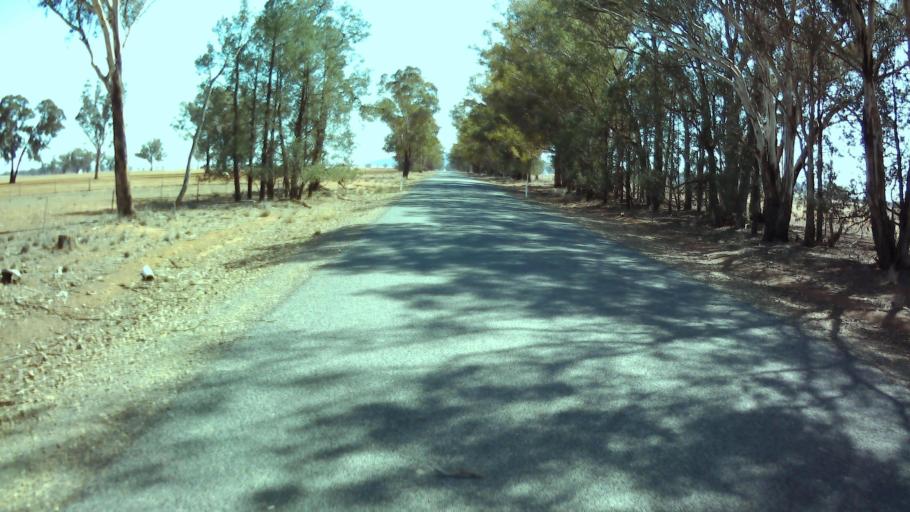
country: AU
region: New South Wales
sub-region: Weddin
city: Grenfell
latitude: -33.7206
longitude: 147.9000
